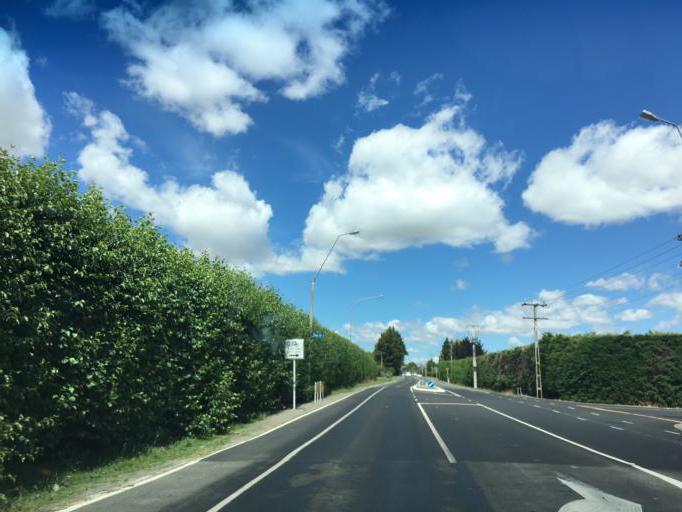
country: NZ
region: Hawke's Bay
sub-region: Hastings District
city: Hastings
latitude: -39.6556
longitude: 176.8722
